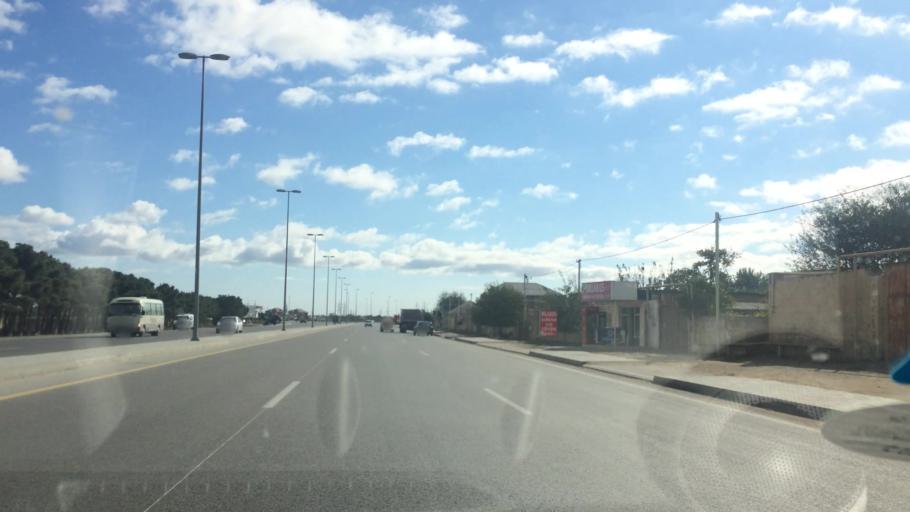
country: AZ
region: Baki
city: Qala
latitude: 40.4459
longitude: 50.1719
